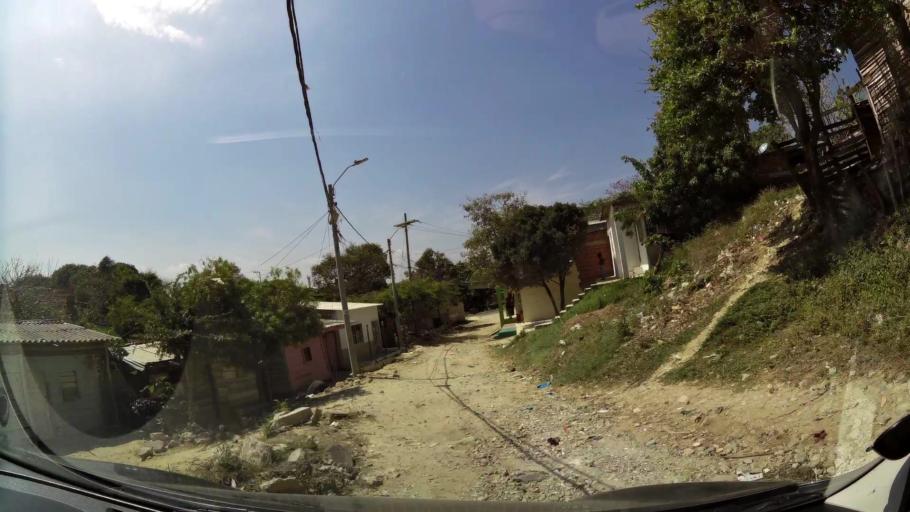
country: CO
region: Atlantico
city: Barranquilla
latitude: 10.9737
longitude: -74.8234
